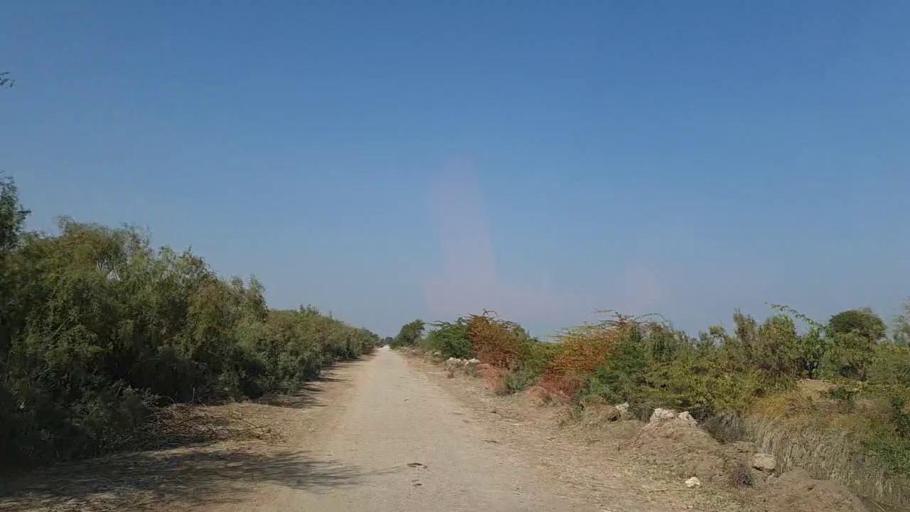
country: PK
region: Sindh
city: Sanghar
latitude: 26.0067
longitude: 69.0553
